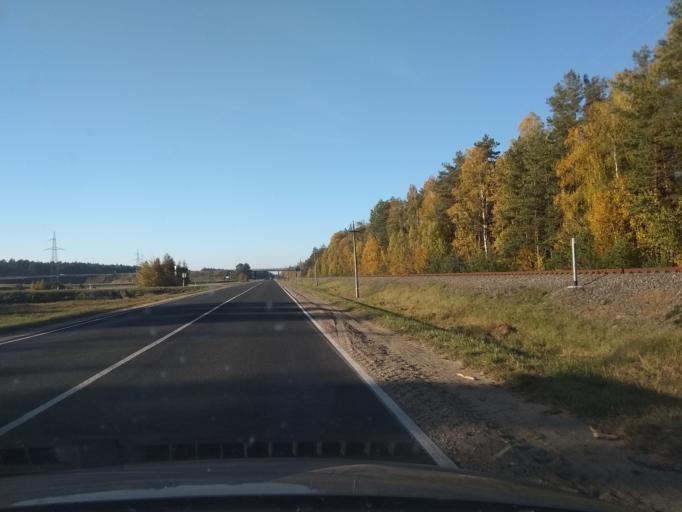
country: BY
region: Brest
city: Nyakhachava
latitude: 52.5724
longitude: 25.1159
